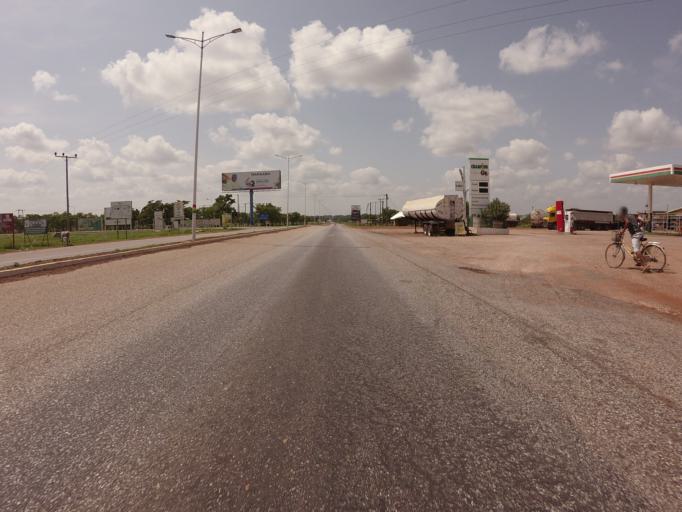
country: GH
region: Northern
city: Savelugu
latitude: 9.5524
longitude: -0.8374
